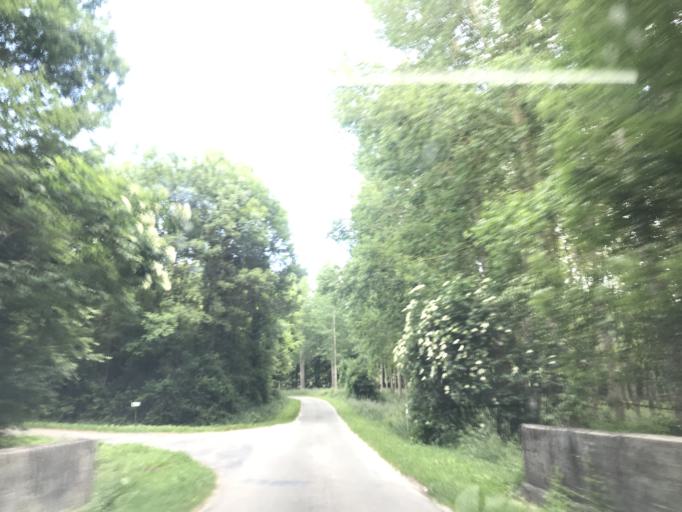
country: FR
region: Aquitaine
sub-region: Departement de la Dordogne
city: Saint-Aulaye
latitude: 45.2646
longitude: 0.1239
